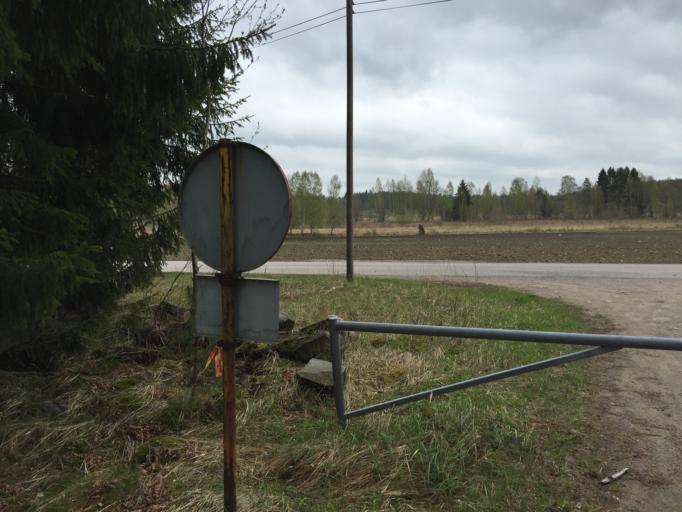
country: SE
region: Soedermanland
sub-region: Vingakers Kommun
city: Vingaker
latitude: 58.9924
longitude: 15.6669
